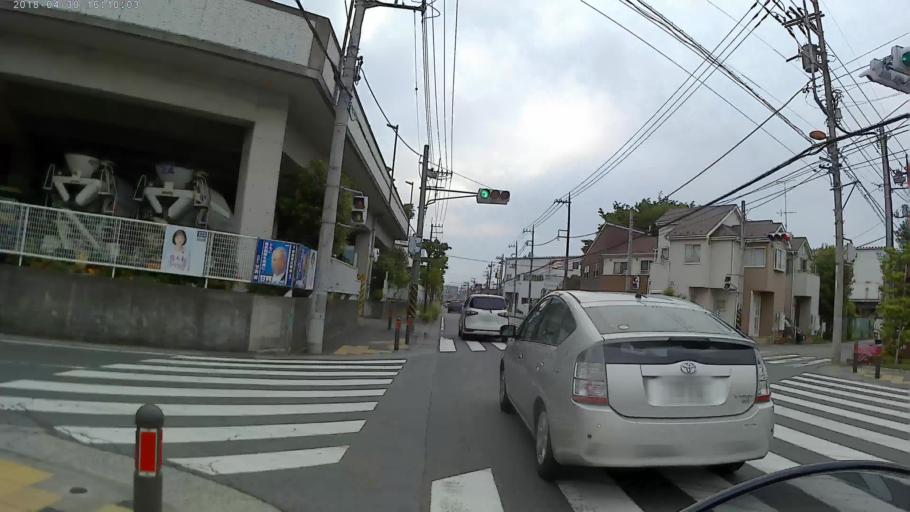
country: JP
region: Kanagawa
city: Minami-rinkan
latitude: 35.5014
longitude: 139.4301
